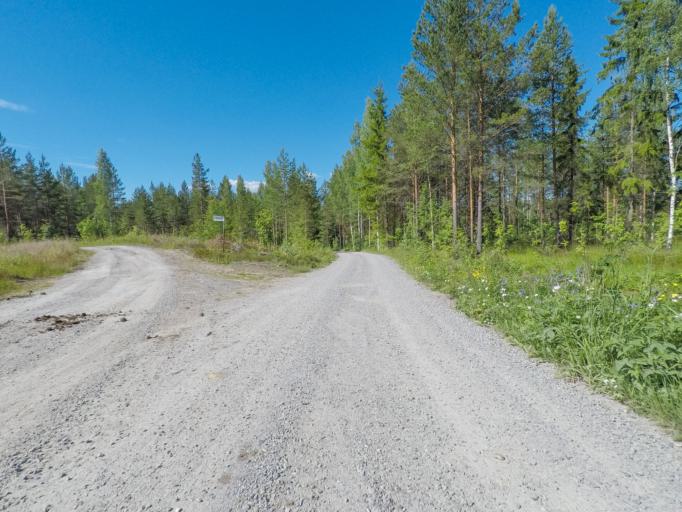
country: FI
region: Northern Savo
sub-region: Varkaus
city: Kangaslampi
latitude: 62.1793
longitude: 28.2217
